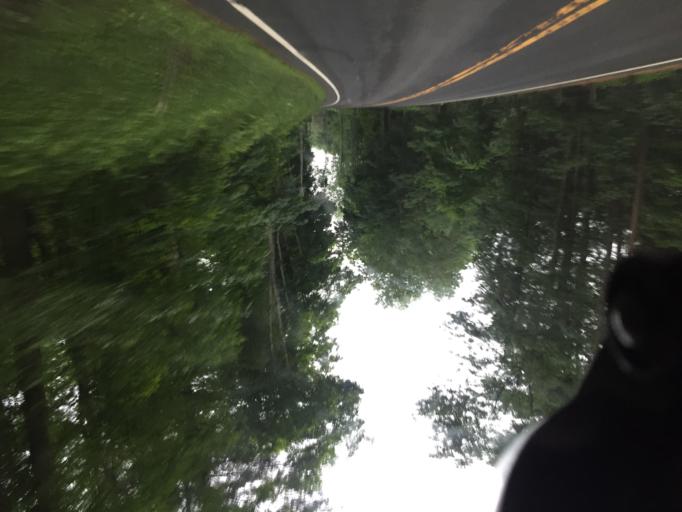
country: US
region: Connecticut
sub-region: Litchfield County
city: Canaan
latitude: 41.9425
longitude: -73.3071
